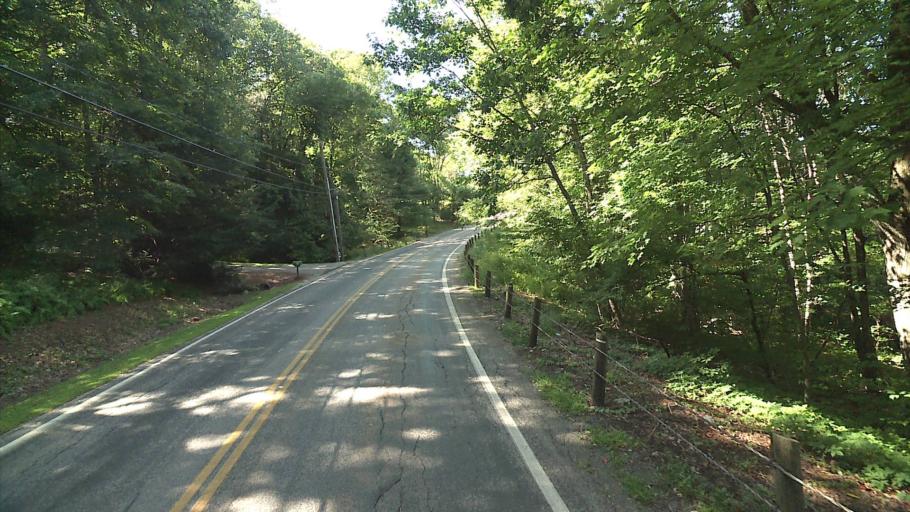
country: US
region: Connecticut
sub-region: Litchfield County
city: Plymouth
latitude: 41.6949
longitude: -73.0579
